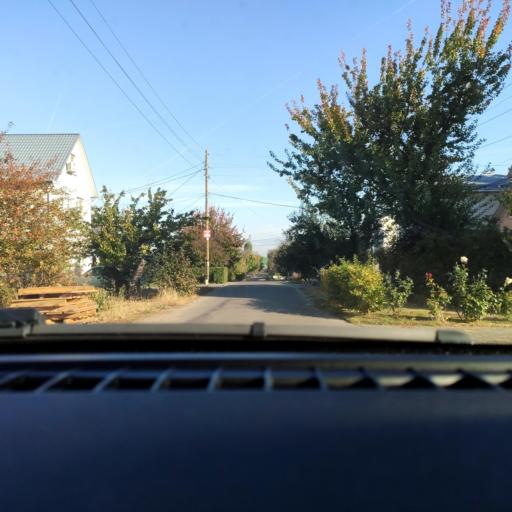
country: RU
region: Voronezj
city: Voronezh
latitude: 51.6645
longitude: 39.2636
